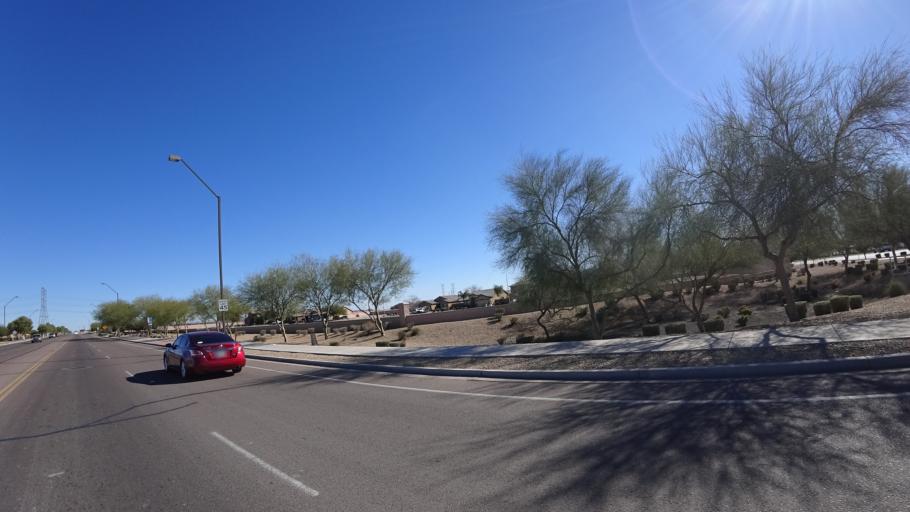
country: US
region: Arizona
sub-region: Maricopa County
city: Avondale
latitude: 33.4205
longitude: -112.3234
